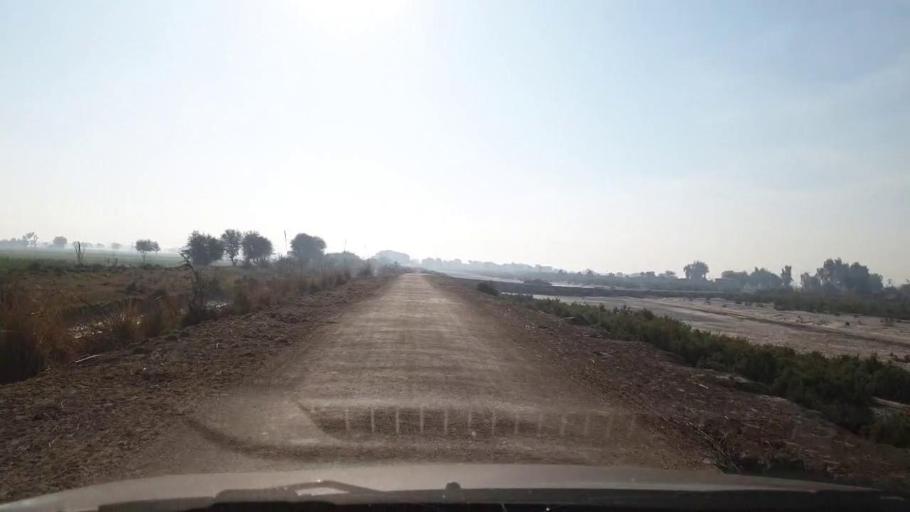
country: PK
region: Sindh
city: Jhol
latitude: 25.9365
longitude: 68.8718
